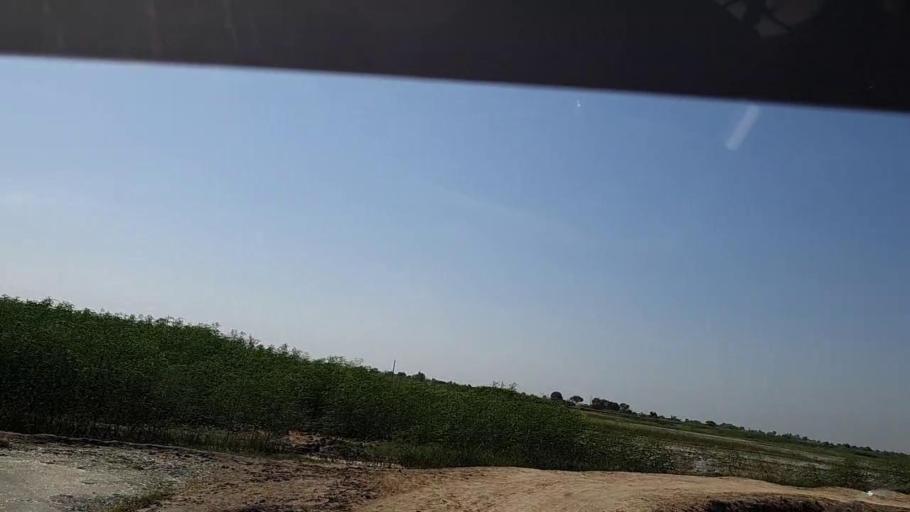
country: PK
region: Sindh
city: Tangwani
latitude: 28.3217
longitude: 69.0872
